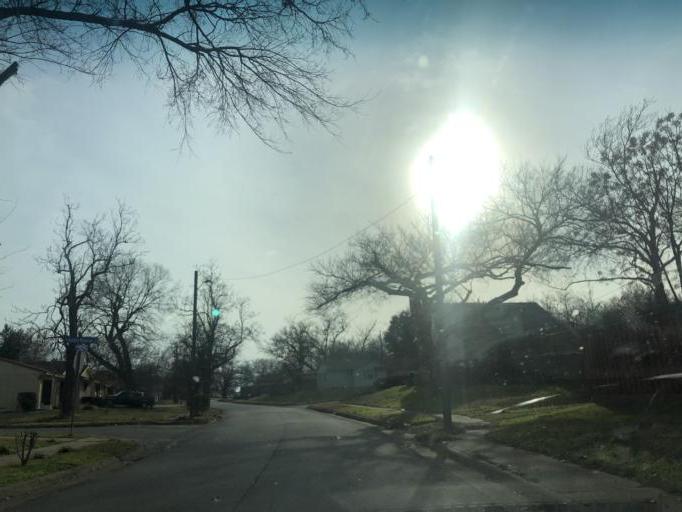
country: US
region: Texas
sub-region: Dallas County
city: Duncanville
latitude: 32.6672
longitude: -96.8979
